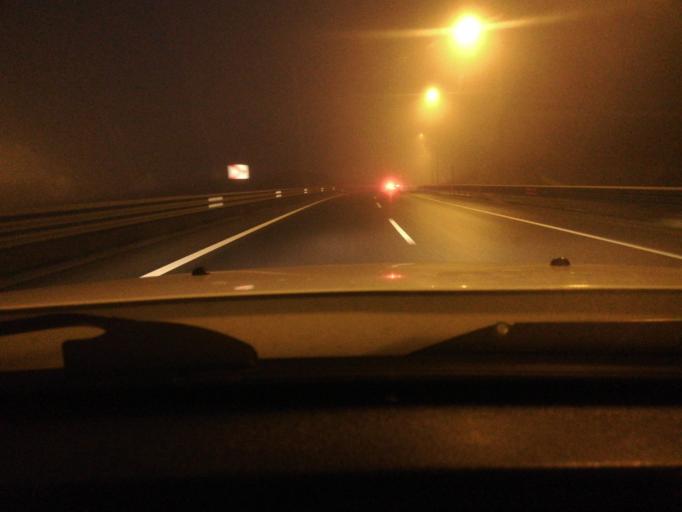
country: TR
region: Istanbul
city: Sultanbeyli
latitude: 40.9749
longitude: 29.3266
